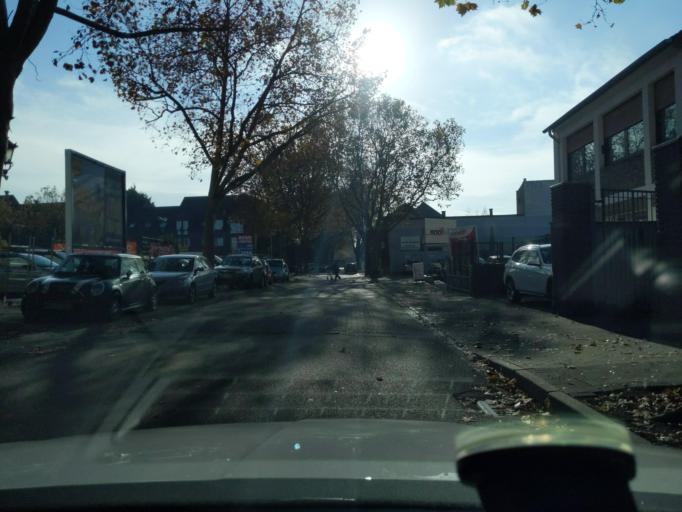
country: DE
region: North Rhine-Westphalia
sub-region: Regierungsbezirk Dusseldorf
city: Willich
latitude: 51.2634
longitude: 6.5508
